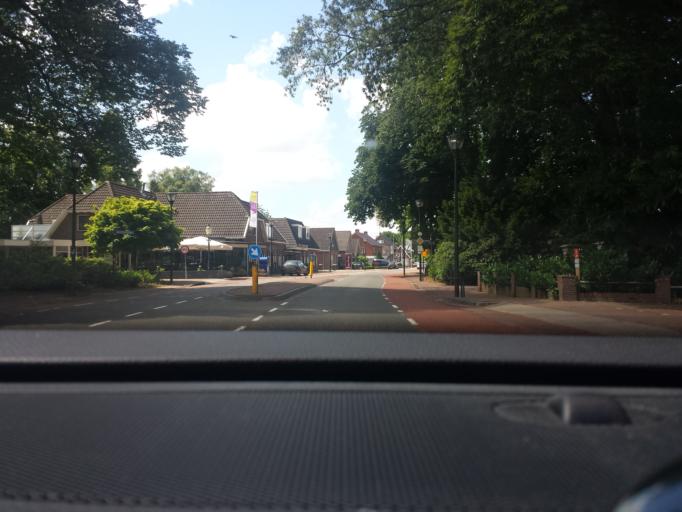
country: NL
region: Overijssel
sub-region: Gemeente Hof van Twente
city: Hengevelde
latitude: 52.2005
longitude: 6.6381
